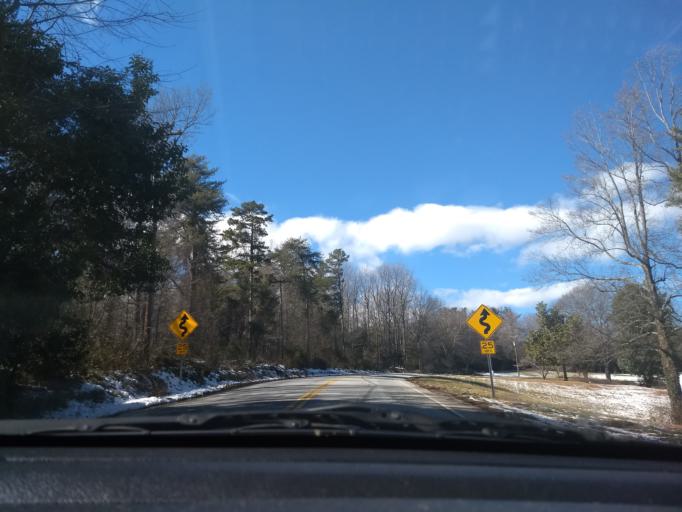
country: US
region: South Carolina
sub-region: Greenville County
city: Greenville
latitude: 34.8953
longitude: -82.3789
